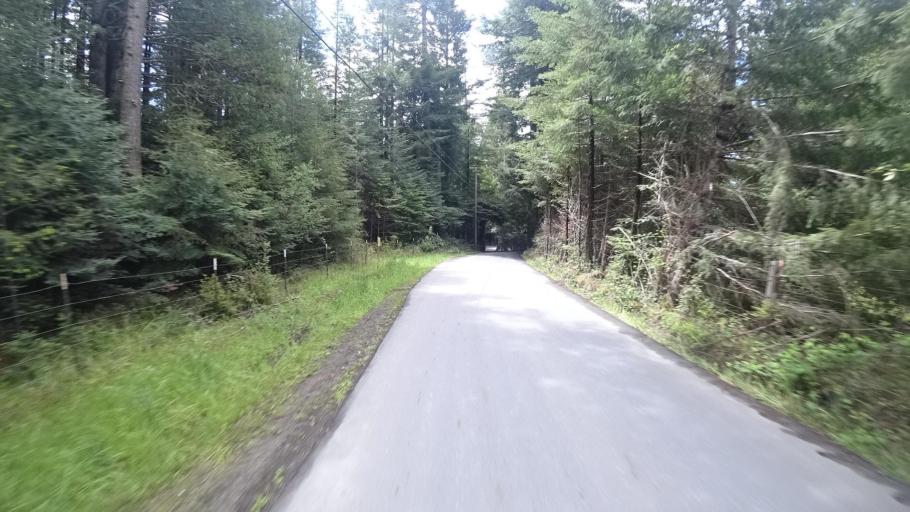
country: US
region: California
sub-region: Humboldt County
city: Blue Lake
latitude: 40.9011
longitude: -123.9878
